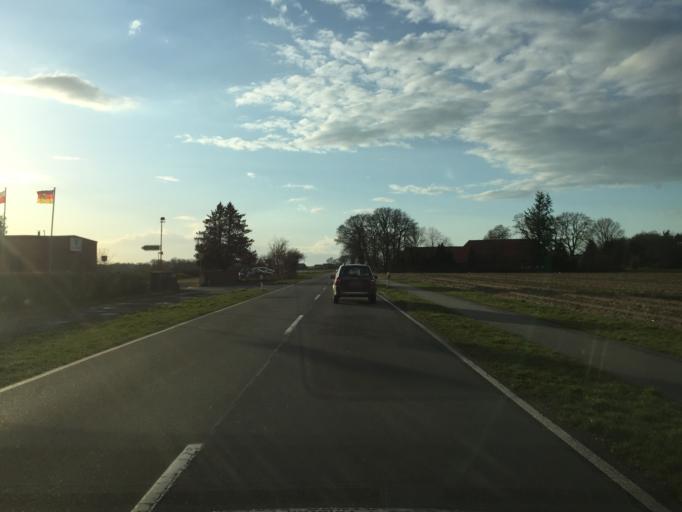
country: DE
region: Lower Saxony
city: Steyerberg
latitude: 52.5656
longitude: 9.0071
